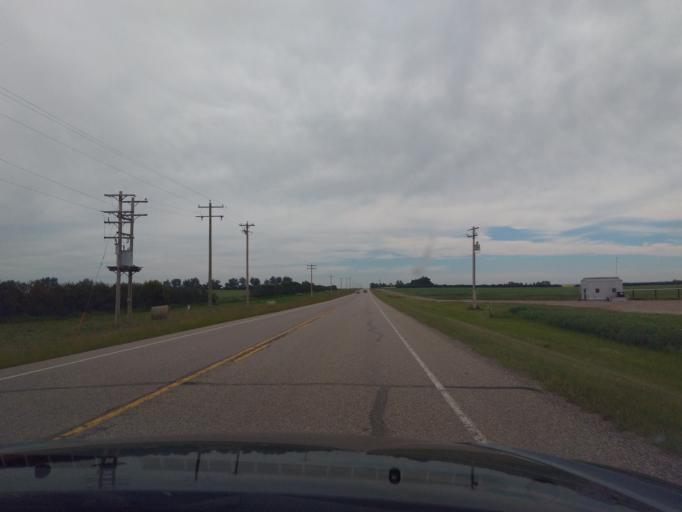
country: CA
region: Alberta
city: Irricana
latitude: 51.5034
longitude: -113.6371
